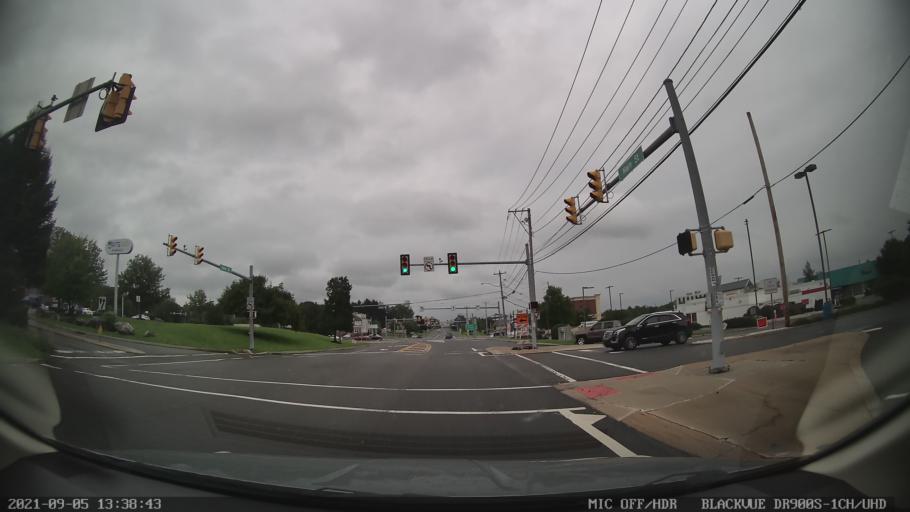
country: US
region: Pennsylvania
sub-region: Lehigh County
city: Trexlertown
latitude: 40.5842
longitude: -75.6280
